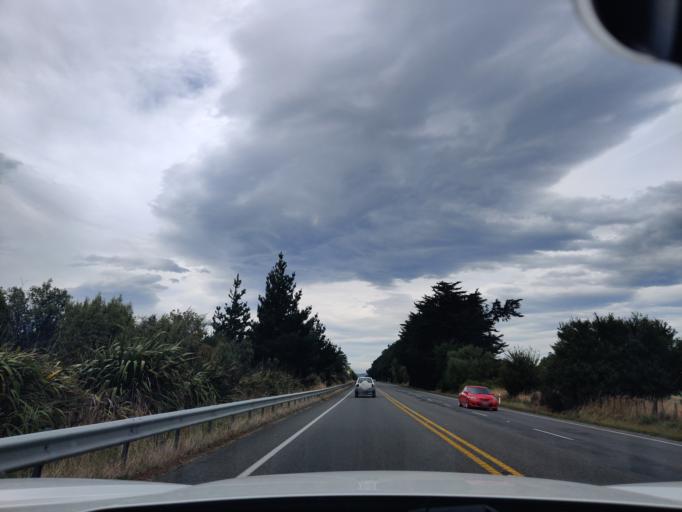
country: NZ
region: Wellington
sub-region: Masterton District
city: Masterton
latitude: -40.9756
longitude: 175.5934
